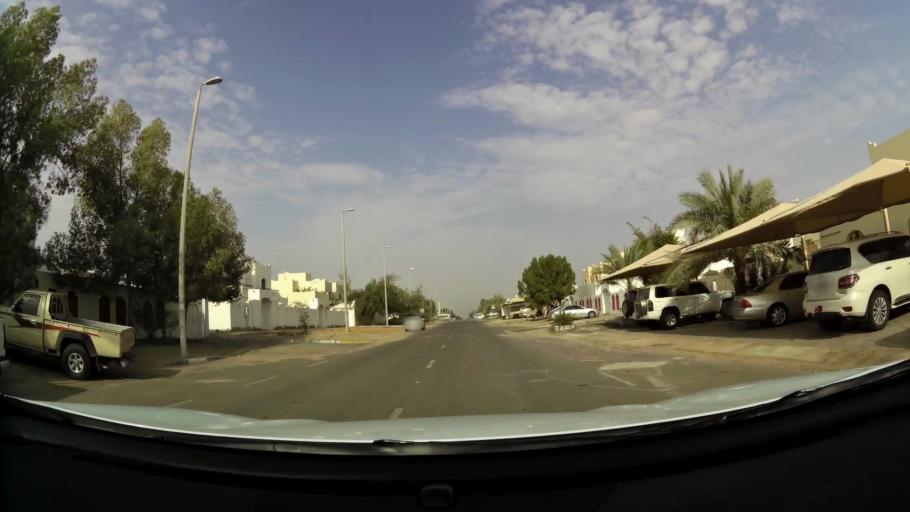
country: AE
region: Abu Dhabi
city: Abu Dhabi
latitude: 24.2385
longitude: 54.7243
